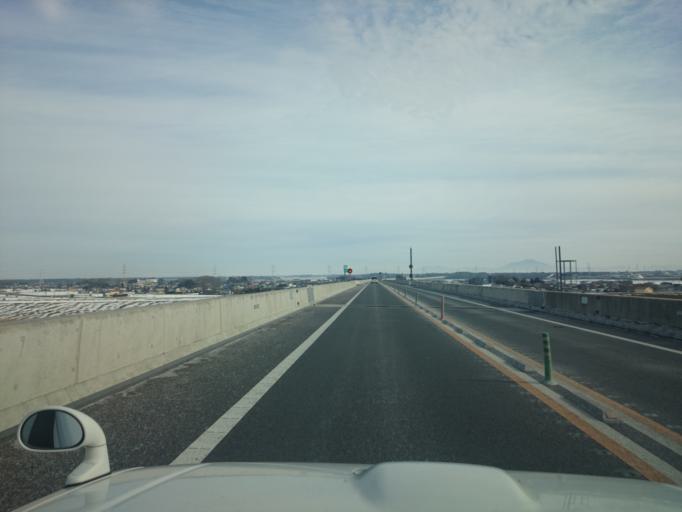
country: JP
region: Ibaraki
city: Sakai
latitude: 36.1171
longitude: 139.7680
